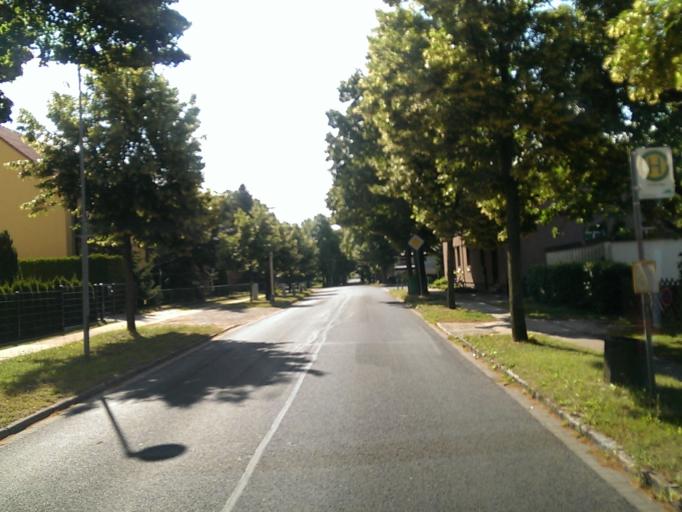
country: DE
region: Brandenburg
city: Grossbeeren
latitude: 52.3164
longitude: 13.3123
